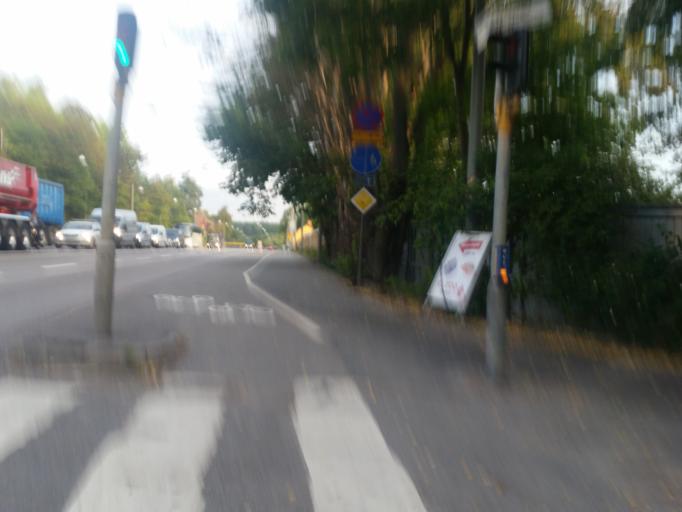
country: SE
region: Stockholm
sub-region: Sundbybergs Kommun
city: Sundbyberg
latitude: 59.3379
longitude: 17.9654
